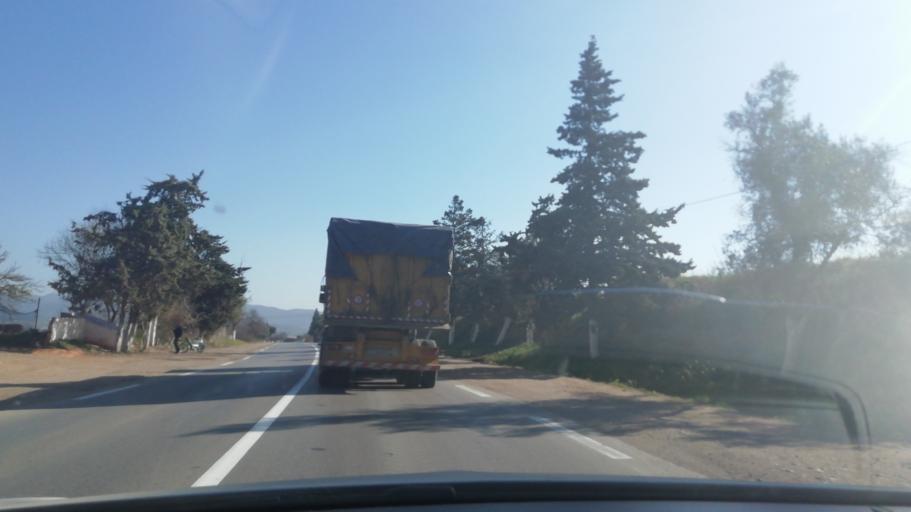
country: DZ
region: Tlemcen
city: Nedroma
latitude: 35.0842
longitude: -1.7980
